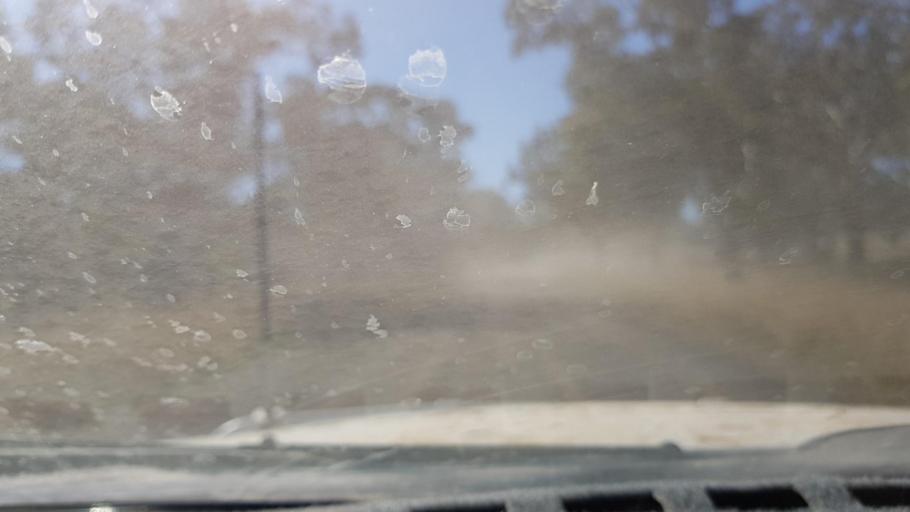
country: AU
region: New South Wales
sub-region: Narrabri
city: Blair Athol
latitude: -30.4201
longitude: 150.4586
